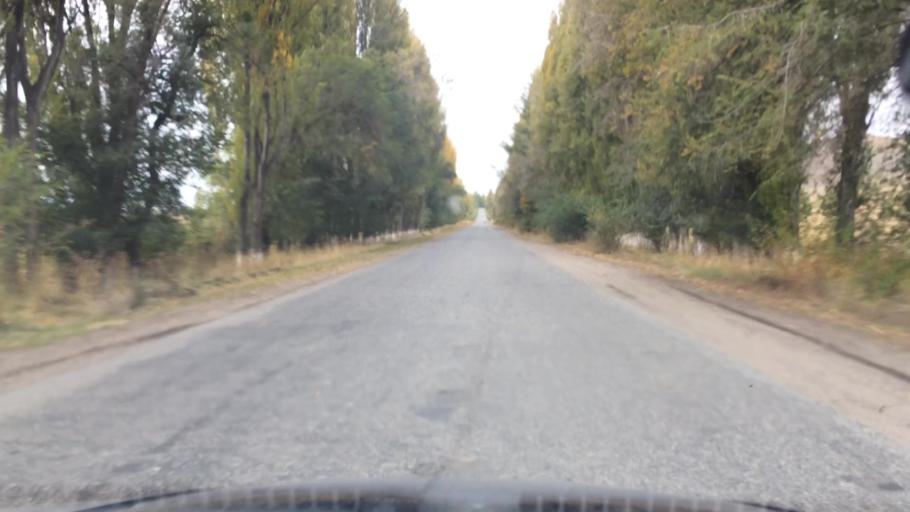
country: KG
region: Ysyk-Koel
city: Pokrovka
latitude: 42.7392
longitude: 77.8958
